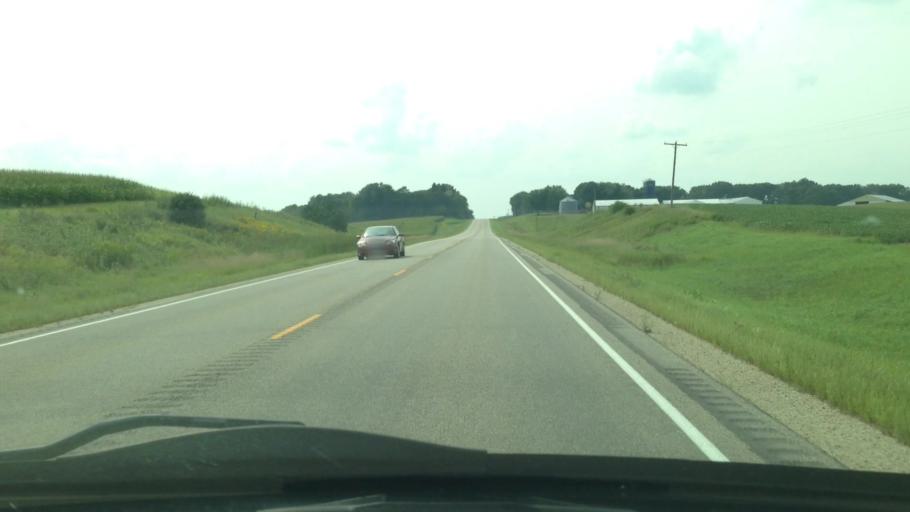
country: US
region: Minnesota
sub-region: Wabasha County
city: Plainview
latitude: 44.1653
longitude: -92.2089
